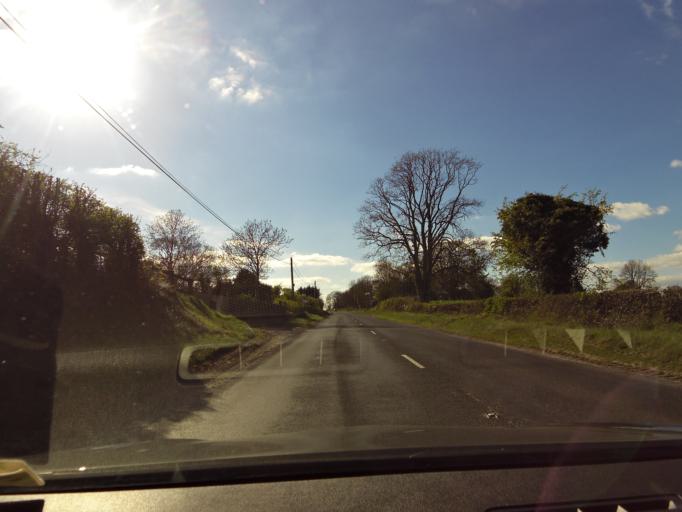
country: IE
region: Leinster
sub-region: Uibh Fhaili
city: Birr
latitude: 53.1011
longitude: -7.9926
